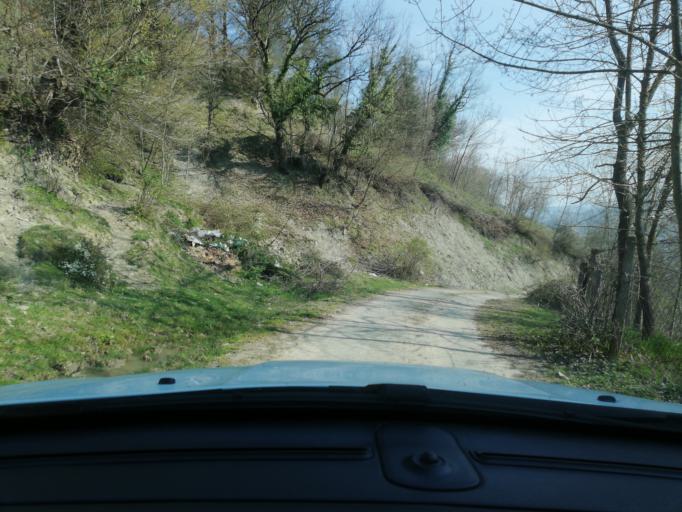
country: TR
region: Karabuk
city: Yenice
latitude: 41.2707
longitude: 32.3586
